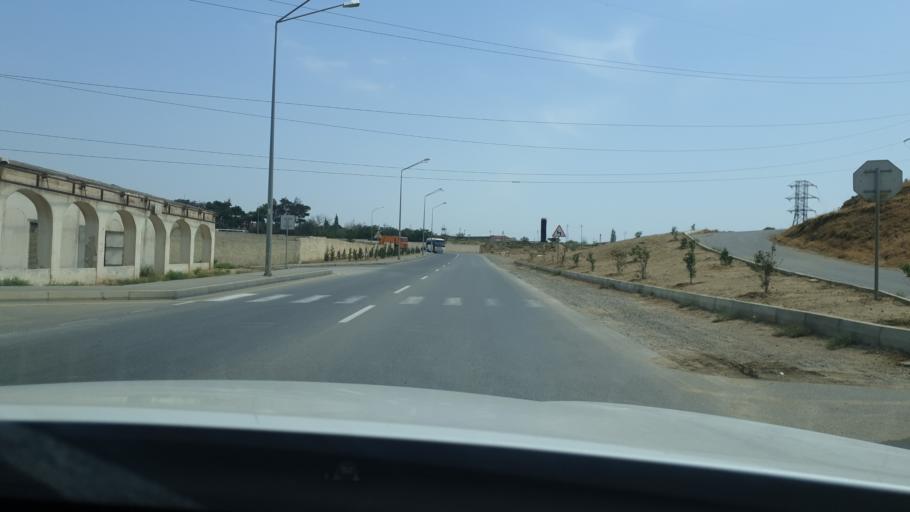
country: AZ
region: Baki
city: Qaracuxur
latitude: 40.3923
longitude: 49.9863
